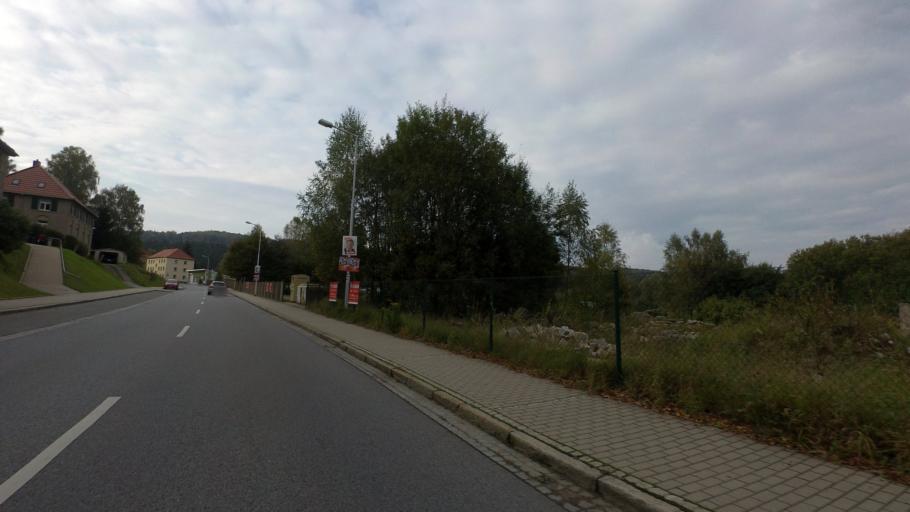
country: DE
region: Saxony
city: Sebnitz
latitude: 50.9806
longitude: 14.2760
